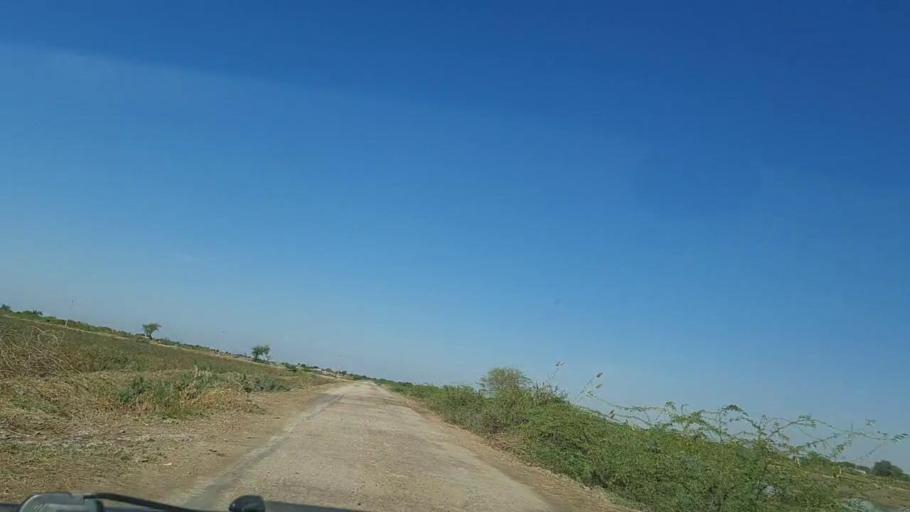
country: PK
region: Sindh
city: Dhoro Naro
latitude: 25.5422
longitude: 69.4996
